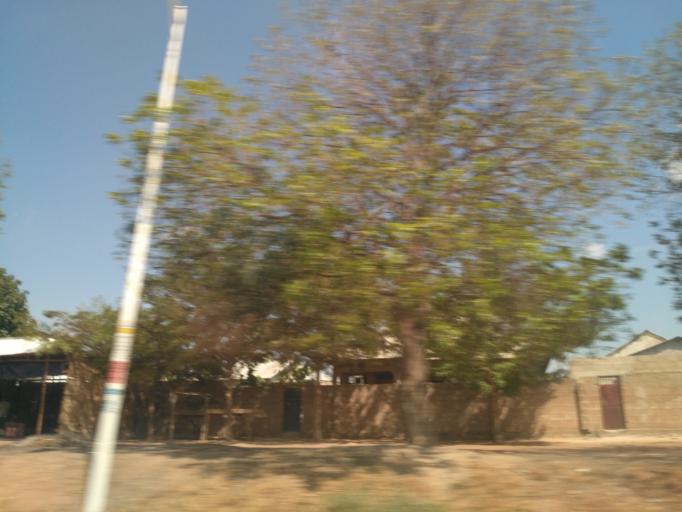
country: TZ
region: Dodoma
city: Dodoma
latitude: -6.1579
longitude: 35.7215
